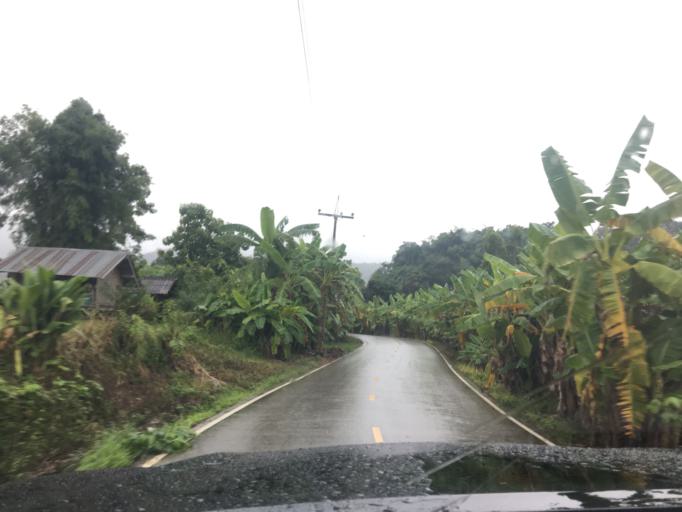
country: TH
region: Chiang Rai
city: Chiang Khong
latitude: 20.2993
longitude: 100.2539
